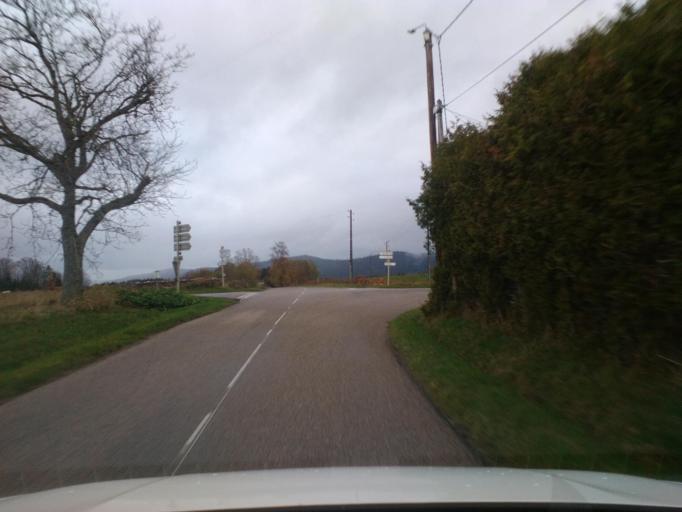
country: FR
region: Lorraine
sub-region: Departement des Vosges
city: Senones
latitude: 48.3611
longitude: 6.9741
